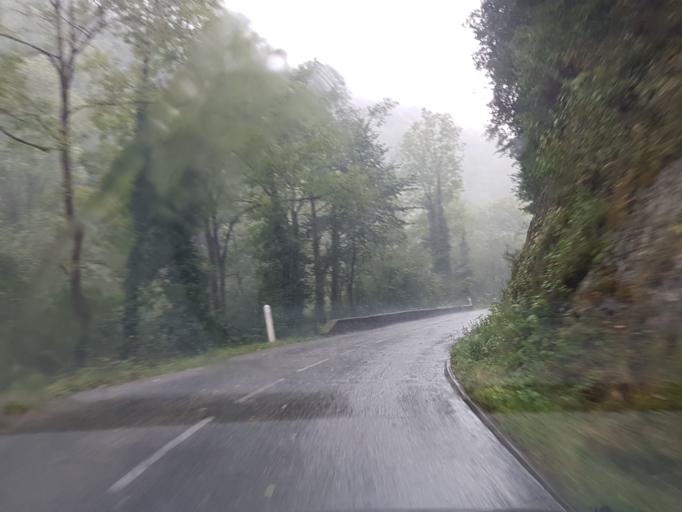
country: FR
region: Midi-Pyrenees
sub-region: Departement de l'Ariege
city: Saint-Girons
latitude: 42.9080
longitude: 1.2921
